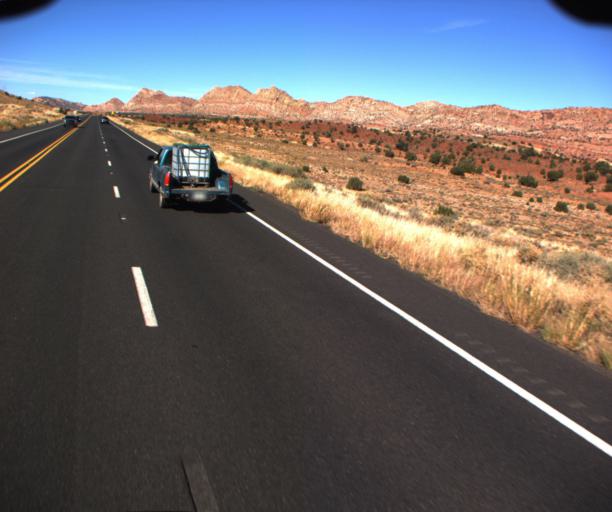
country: US
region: Arizona
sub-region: Coconino County
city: Tuba City
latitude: 36.3510
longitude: -111.5055
